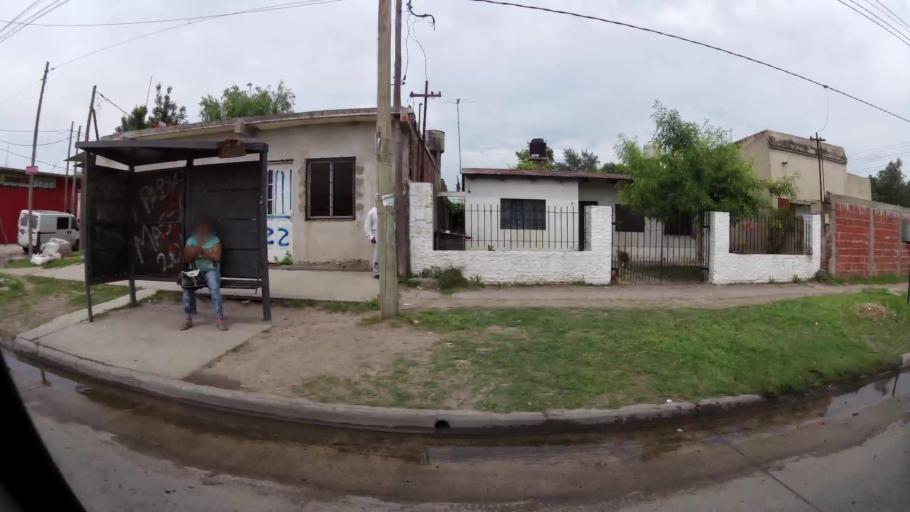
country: AR
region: Buenos Aires
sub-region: Partido de La Plata
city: La Plata
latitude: -34.9317
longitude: -58.0105
